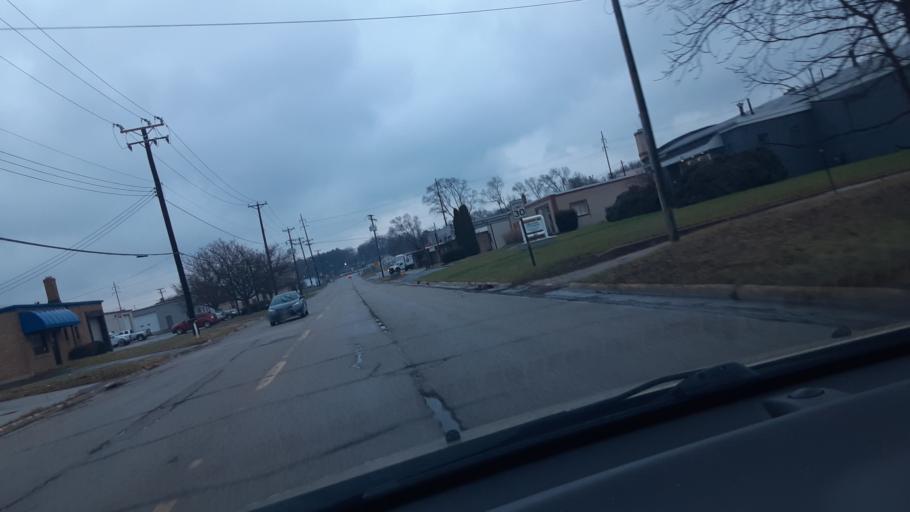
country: US
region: Illinois
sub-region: Winnebago County
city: Loves Park
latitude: 42.3107
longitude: -89.0478
